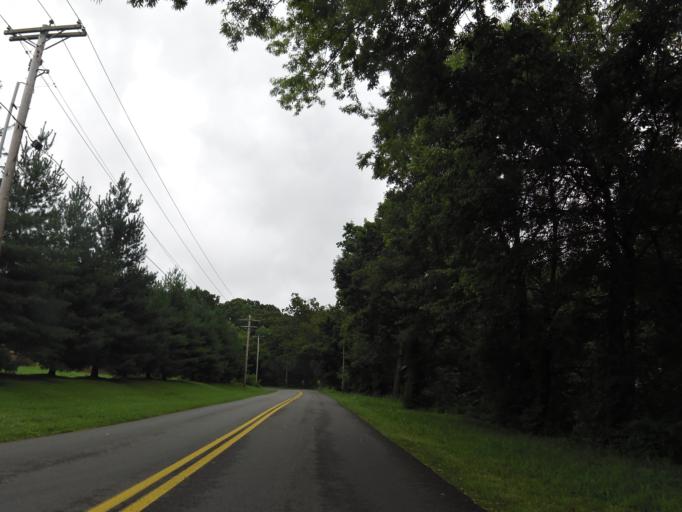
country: US
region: Missouri
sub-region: Cape Girardeau County
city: Cape Girardeau
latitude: 37.3562
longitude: -89.5629
